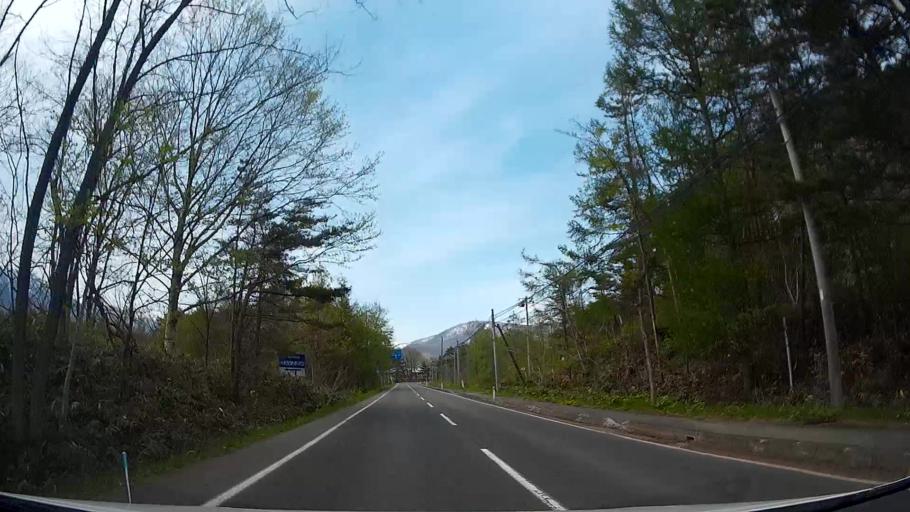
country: JP
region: Iwate
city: Shizukuishi
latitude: 39.9228
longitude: 140.9830
